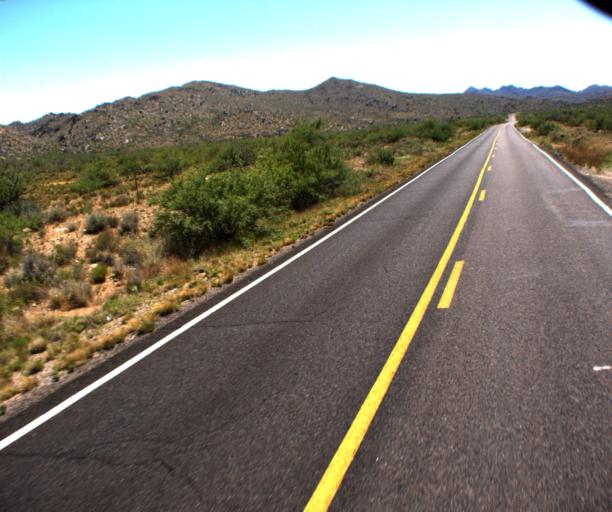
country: US
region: Arizona
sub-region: Yavapai County
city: Bagdad
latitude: 34.5170
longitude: -113.1468
